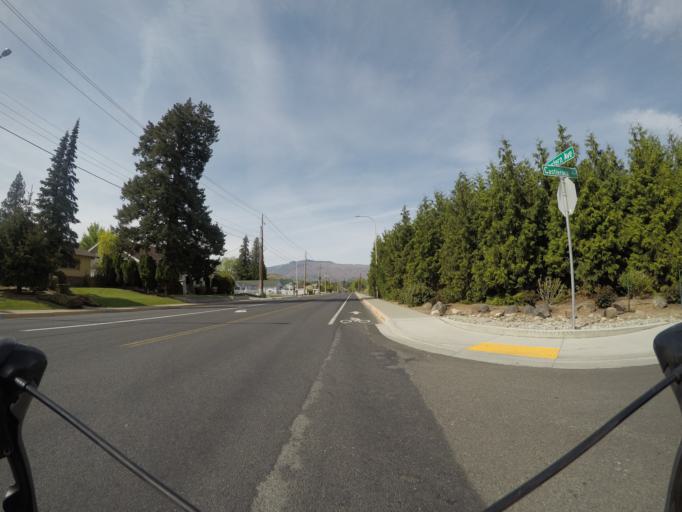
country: US
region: Washington
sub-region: Chelan County
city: West Wenatchee
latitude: 47.4192
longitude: -120.3458
